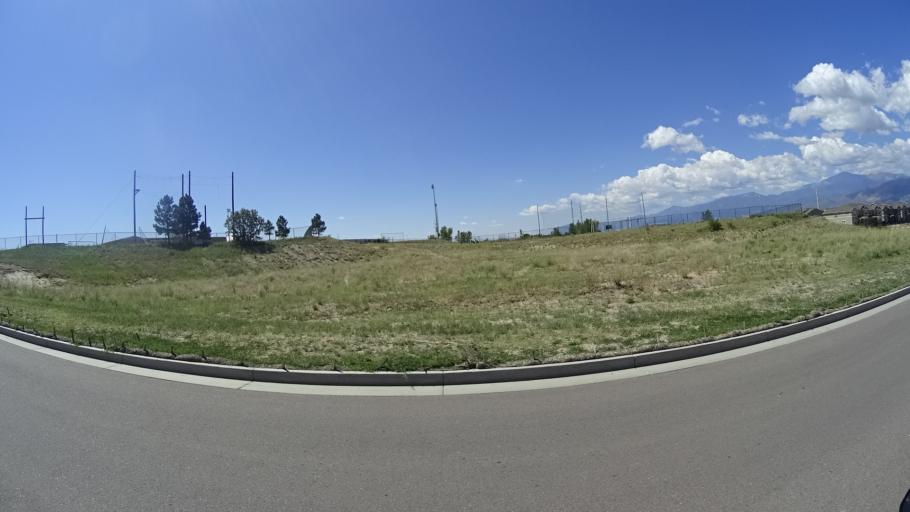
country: US
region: Colorado
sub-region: El Paso County
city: Black Forest
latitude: 38.9890
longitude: -104.7651
